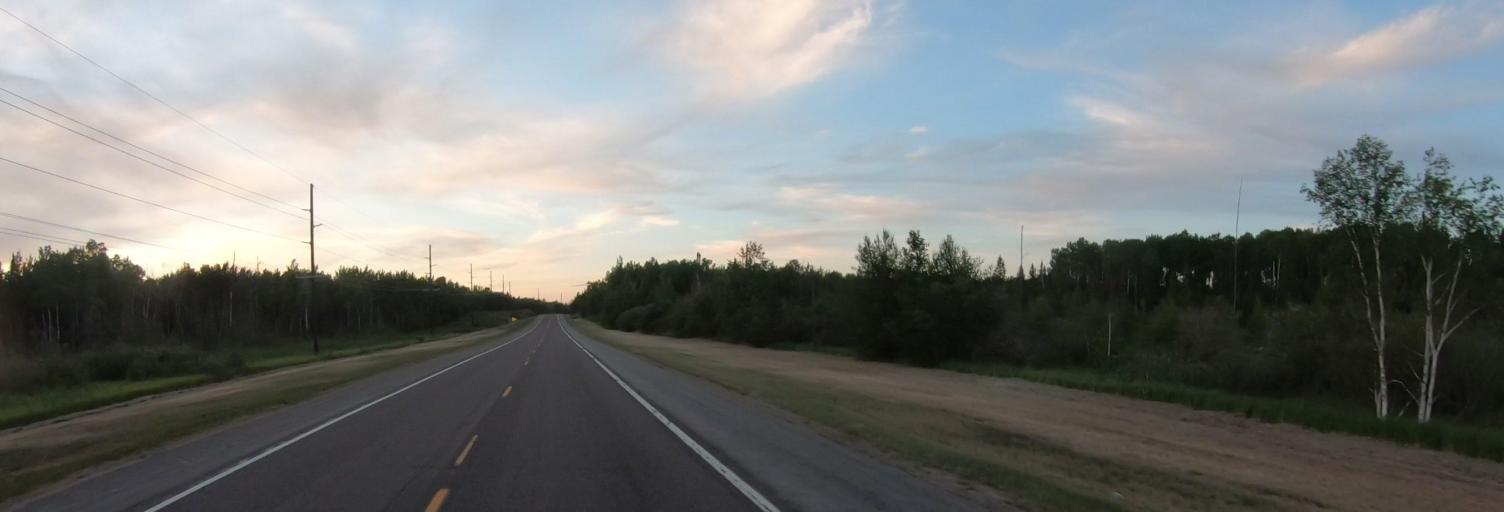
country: US
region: Minnesota
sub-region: Saint Louis County
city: Aurora
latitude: 47.8207
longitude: -92.3713
